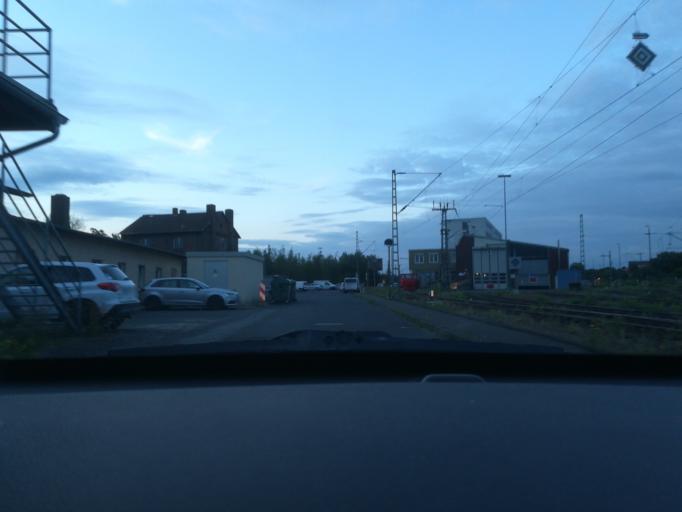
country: DE
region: Hesse
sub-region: Regierungsbezirk Kassel
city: Kassel
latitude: 51.3252
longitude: 9.4663
